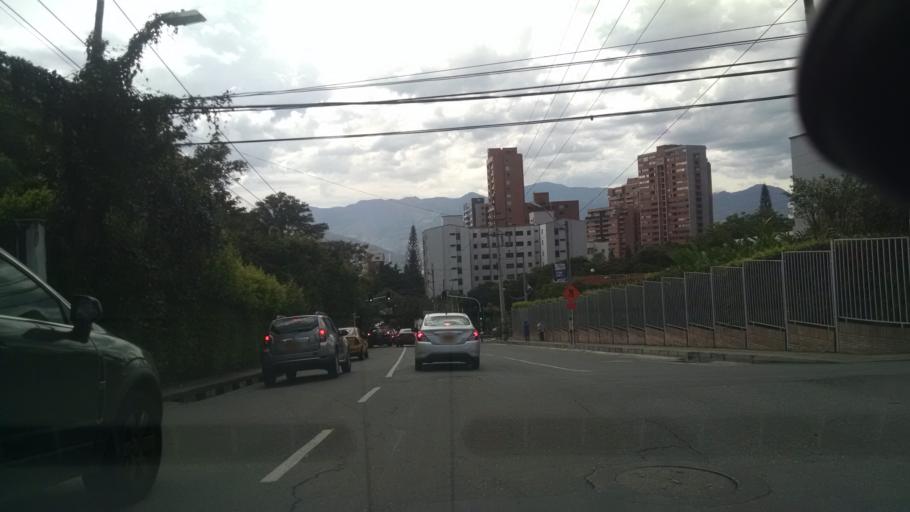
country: CO
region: Antioquia
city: Envigado
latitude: 6.2009
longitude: -75.5653
